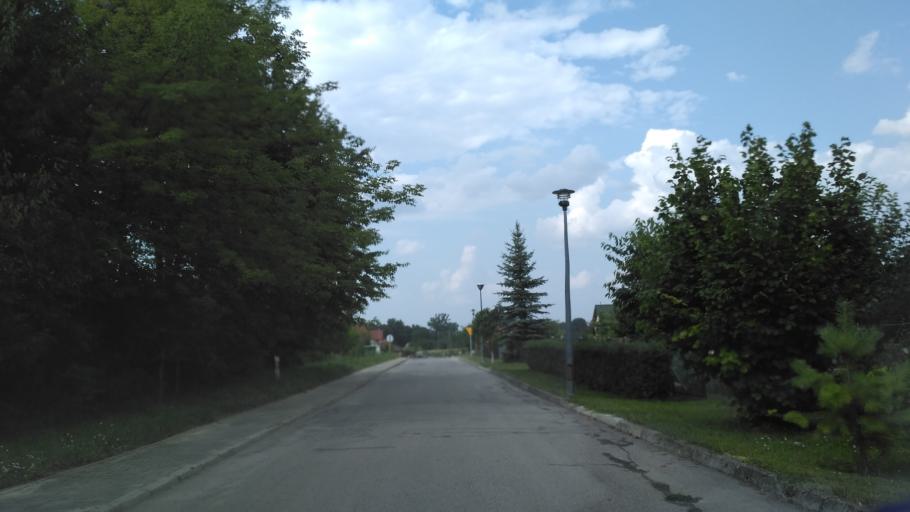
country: PL
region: Lublin Voivodeship
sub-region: Powiat chelmski
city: Rejowiec Fabryczny
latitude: 51.1870
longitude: 23.1663
